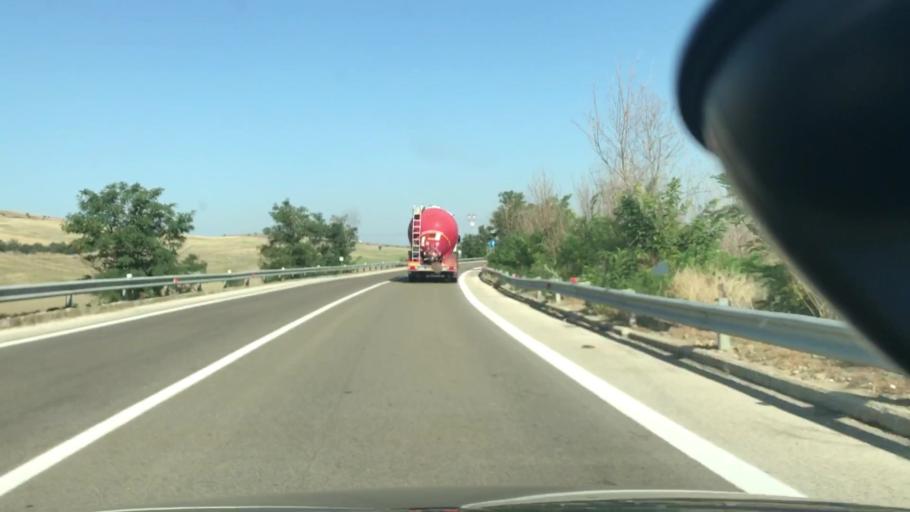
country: IT
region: Basilicate
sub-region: Provincia di Matera
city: Irsina
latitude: 40.7943
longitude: 16.2775
